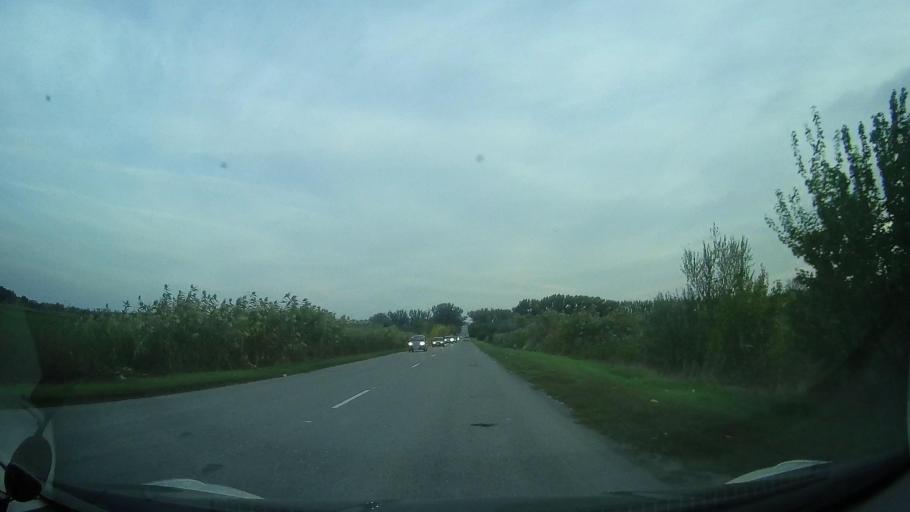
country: RU
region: Rostov
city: Ol'ginskaya
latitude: 47.1296
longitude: 39.9628
